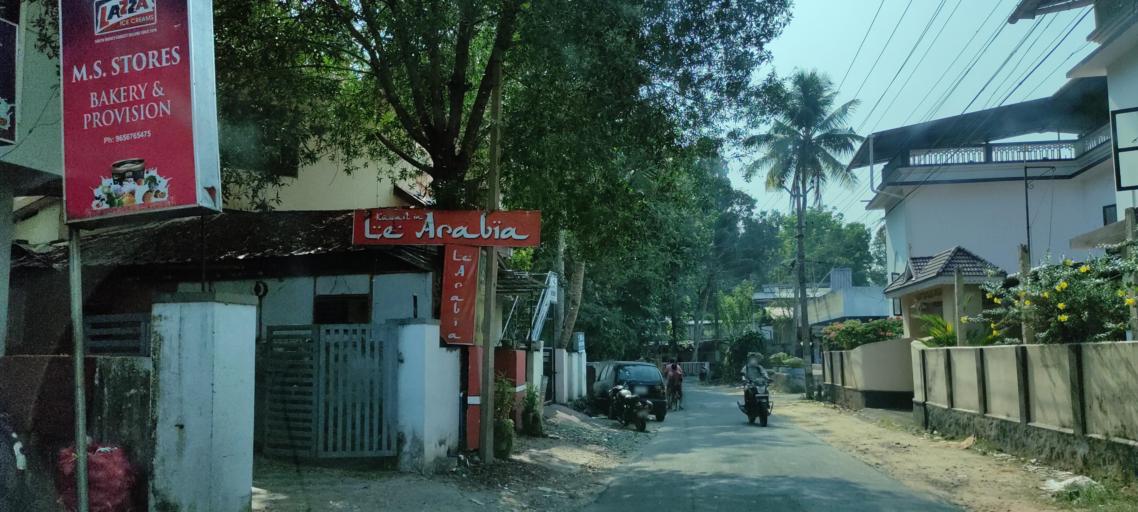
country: IN
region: Kerala
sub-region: Pattanamtitta
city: Tiruvalla
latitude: 9.3462
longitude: 76.5347
